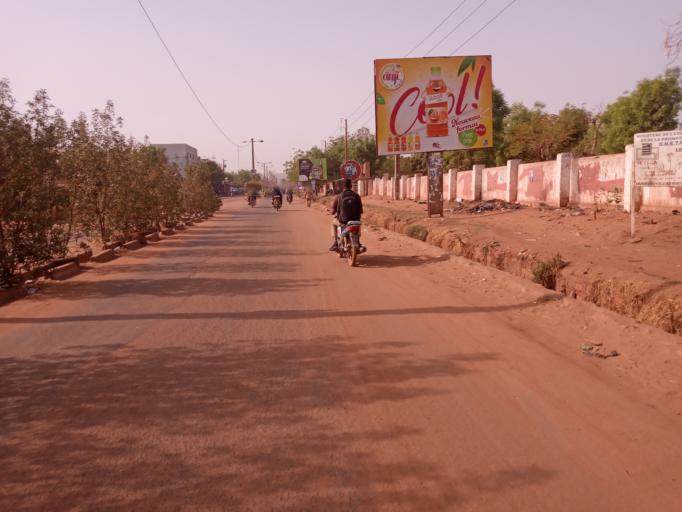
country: ML
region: Bamako
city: Bamako
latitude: 12.6663
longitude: -7.9417
